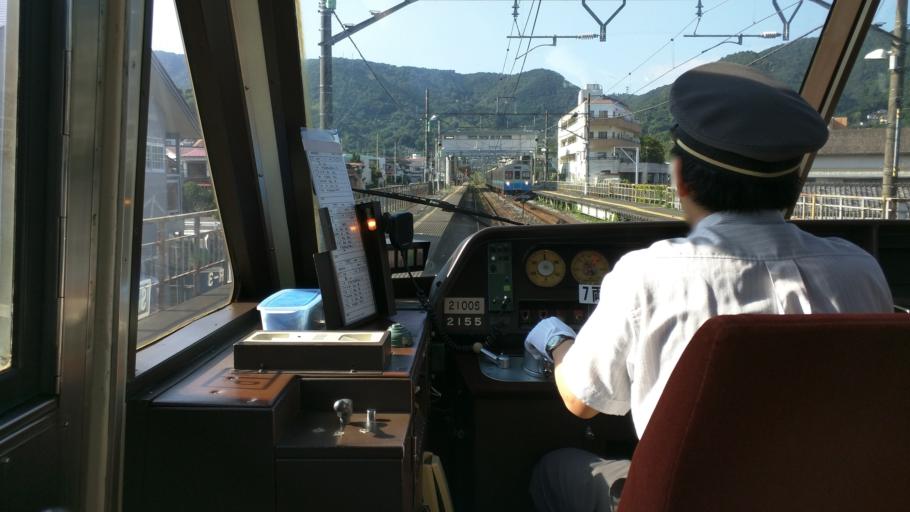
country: JP
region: Shizuoka
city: Ito
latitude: 35.0046
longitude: 139.0800
